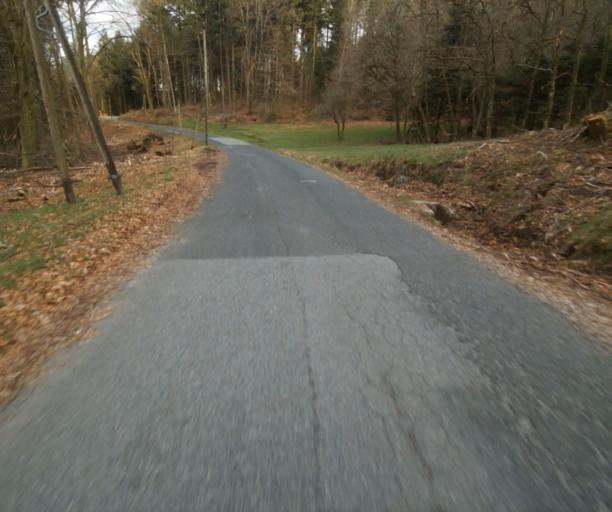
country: FR
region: Limousin
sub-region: Departement de la Correze
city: Correze
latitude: 45.4202
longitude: 1.8870
